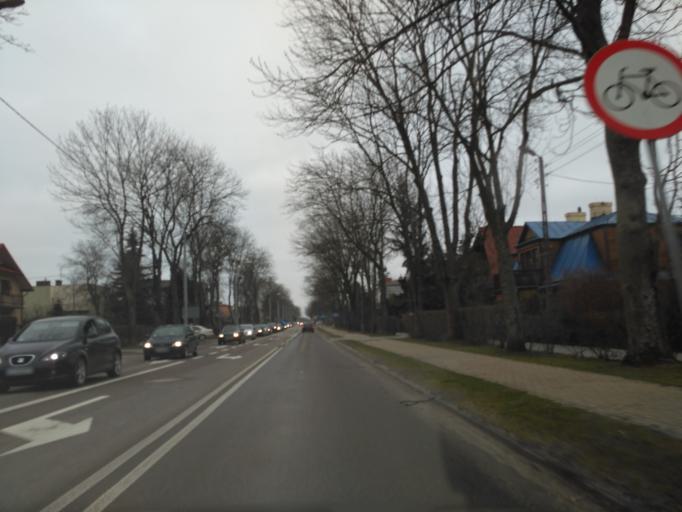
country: PL
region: Lublin Voivodeship
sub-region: Chelm
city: Chelm
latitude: 51.1269
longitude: 23.4900
